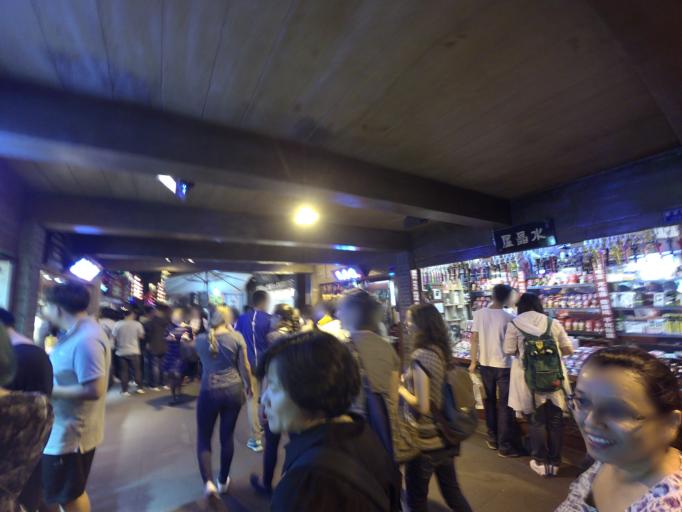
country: CN
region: Sichuan
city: Chengdu
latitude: 30.6488
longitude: 104.0474
